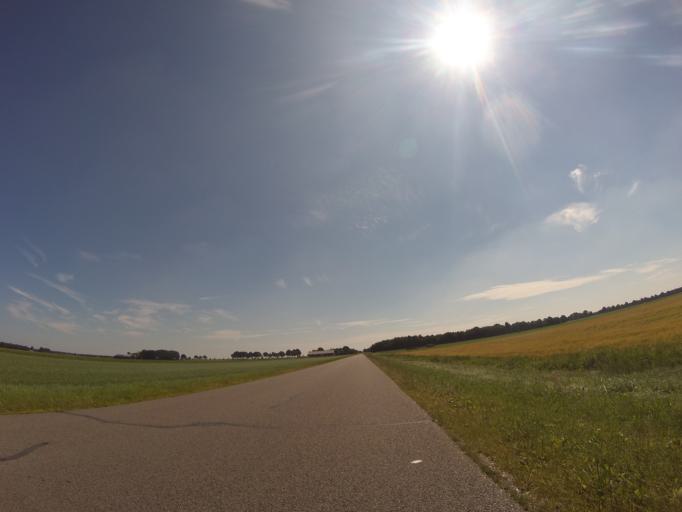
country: NL
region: Drenthe
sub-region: Gemeente Emmen
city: Klazienaveen
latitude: 52.6890
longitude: 6.9678
